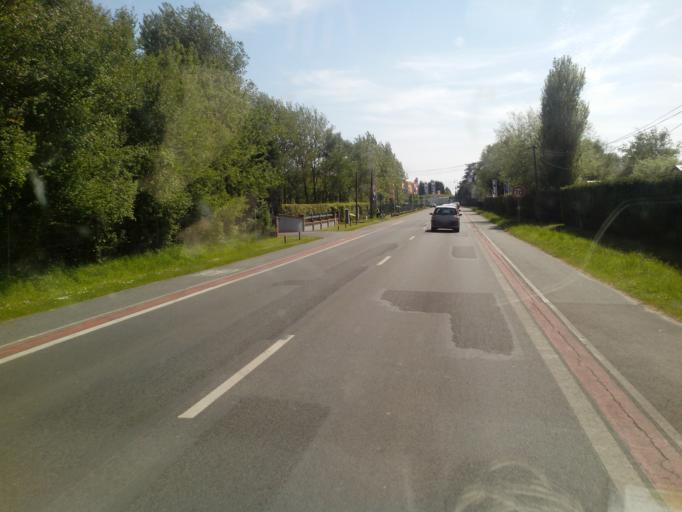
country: FR
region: Nord-Pas-de-Calais
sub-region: Departement du Pas-de-Calais
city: Merlimont
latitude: 50.4334
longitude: 1.6079
